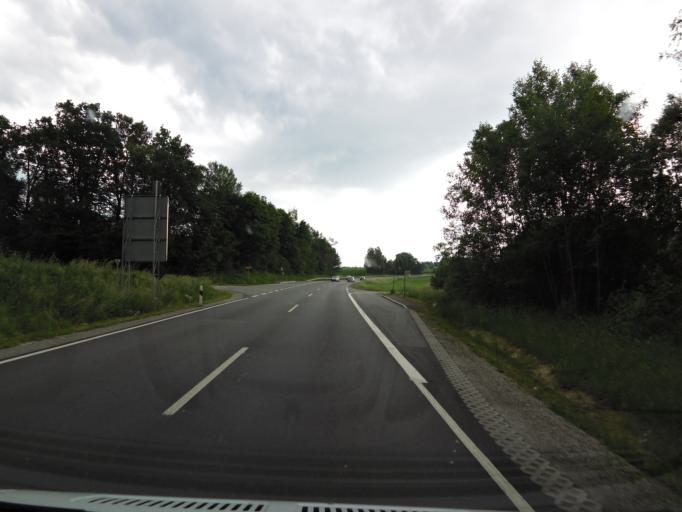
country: DE
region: Bavaria
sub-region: Lower Bavaria
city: Aicha vorm Wald
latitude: 48.6701
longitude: 13.2739
